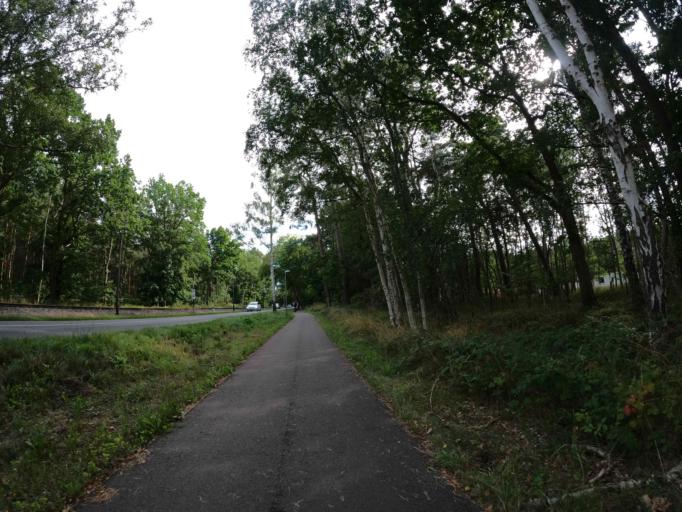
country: DE
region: Mecklenburg-Vorpommern
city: Ostseebad Sellin
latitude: 54.3539
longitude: 13.7030
